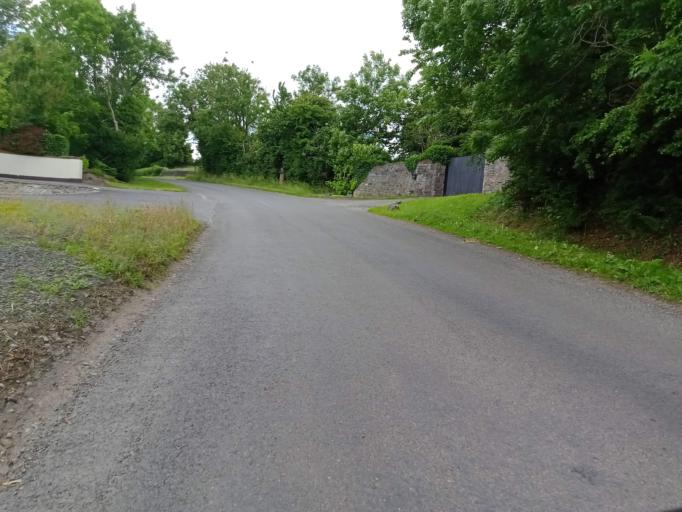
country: IE
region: Leinster
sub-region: Kilkenny
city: Kilkenny
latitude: 52.6922
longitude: -7.2490
